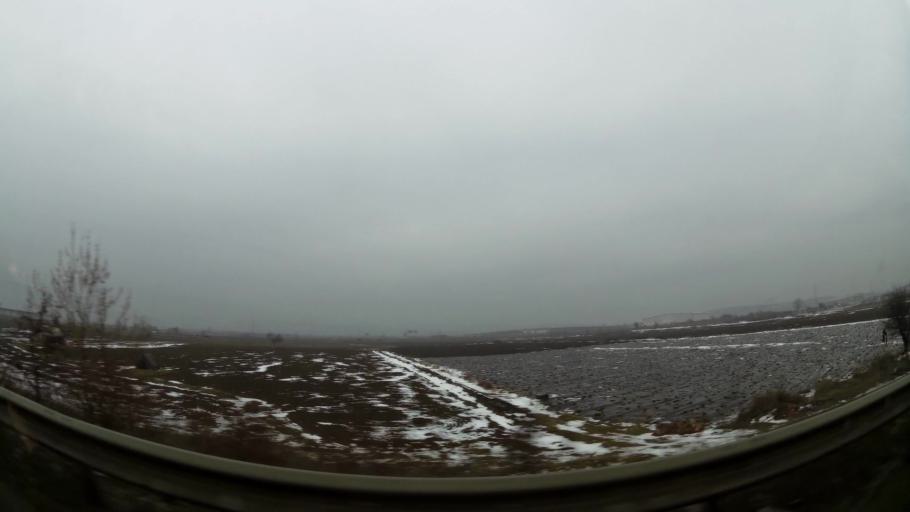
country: MK
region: Suto Orizari
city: Suto Orizare
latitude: 42.0510
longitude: 21.3838
